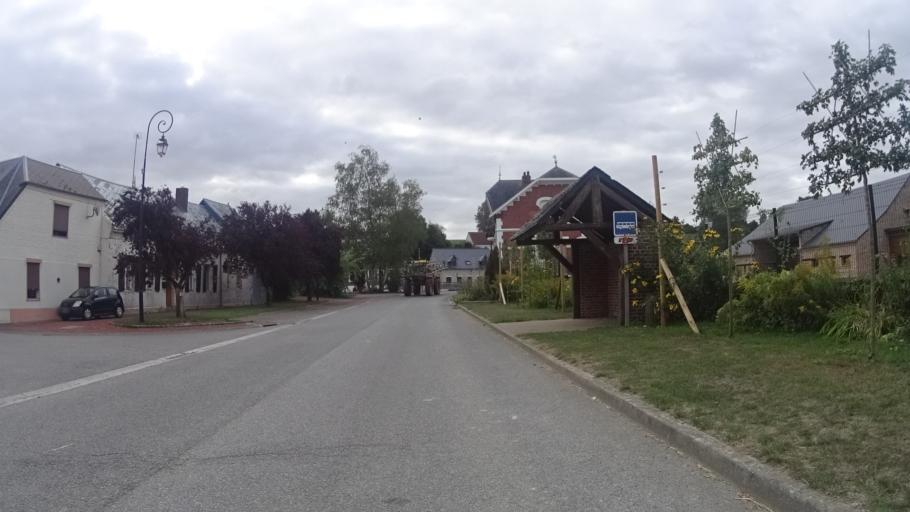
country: FR
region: Picardie
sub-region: Departement de l'Aisne
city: Etreux
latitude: 49.9564
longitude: 3.6083
